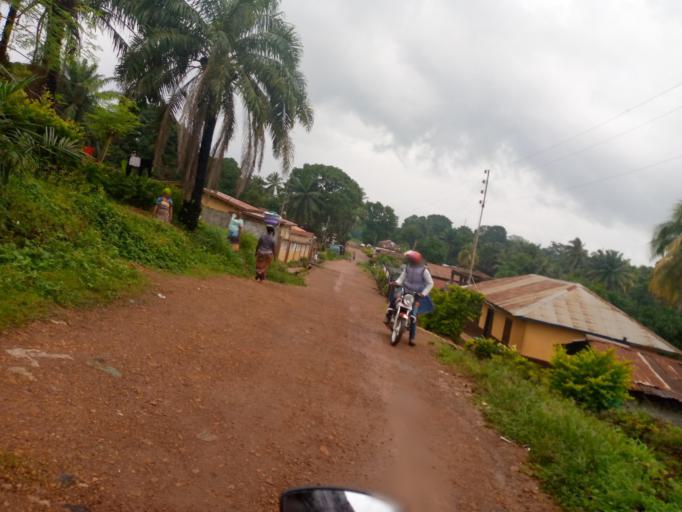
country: SL
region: Eastern Province
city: Kenema
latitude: 7.8802
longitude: -11.1809
